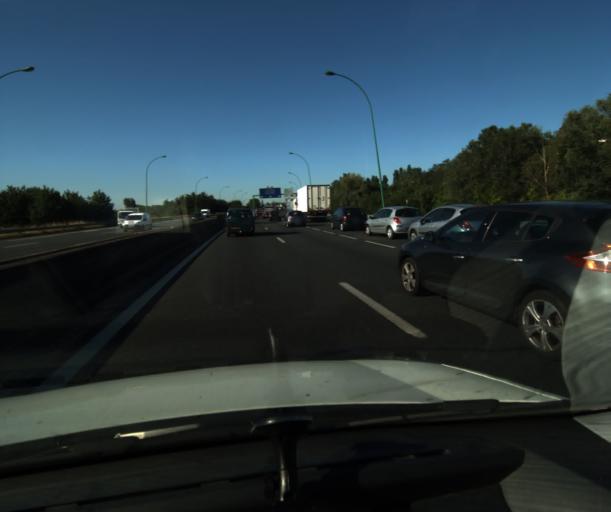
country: FR
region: Midi-Pyrenees
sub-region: Departement de la Haute-Garonne
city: Balma
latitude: 43.5771
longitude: 1.4977
